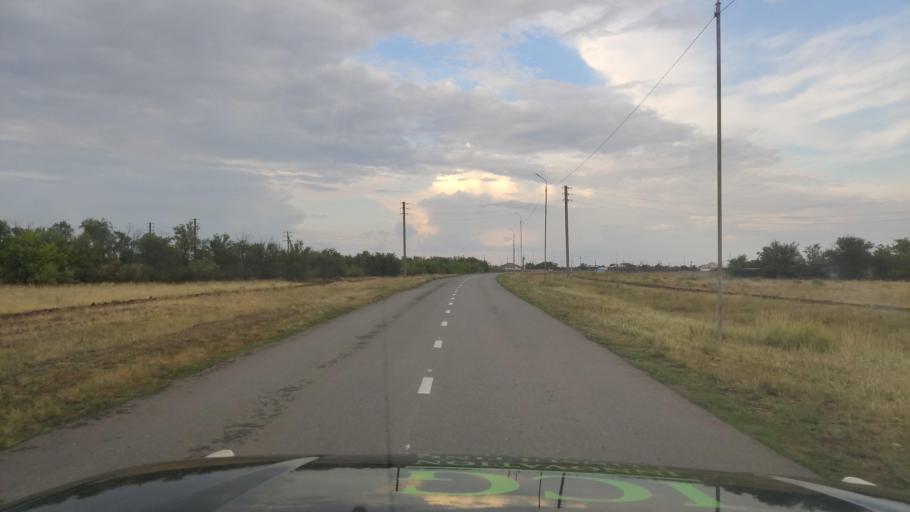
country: KZ
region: Pavlodar
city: Pavlodar
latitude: 52.3428
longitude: 77.2498
